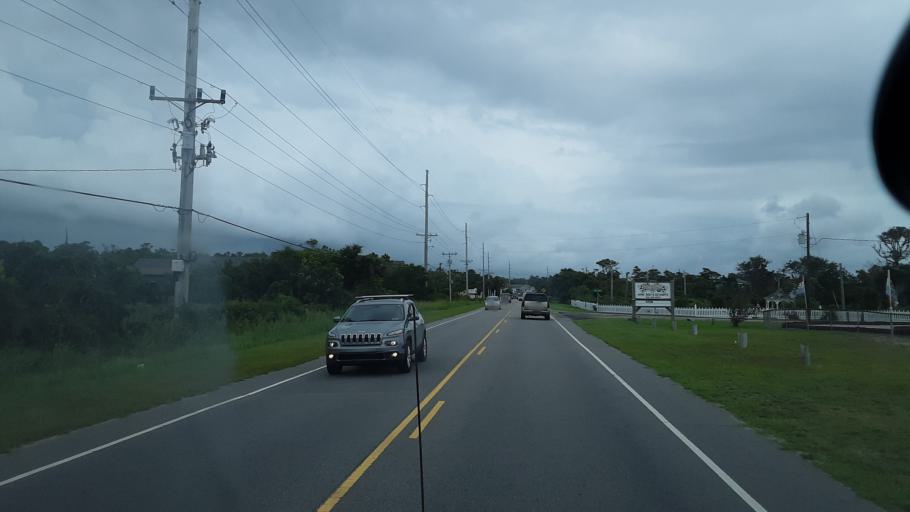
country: US
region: North Carolina
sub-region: Dare County
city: Buxton
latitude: 35.2559
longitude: -75.5906
